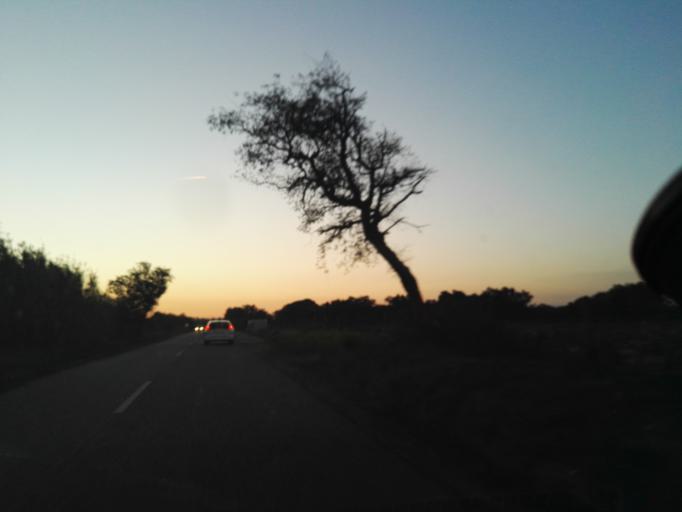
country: PT
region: Setubal
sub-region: Alcochete
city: Alcochete
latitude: 38.7282
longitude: -8.9151
